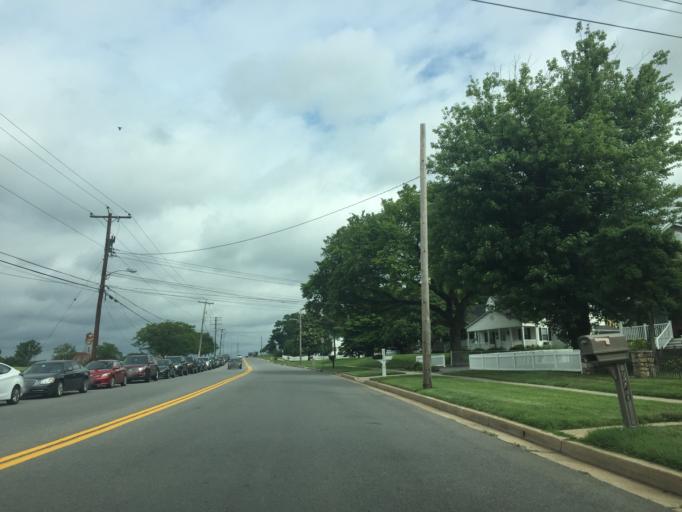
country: US
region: Maryland
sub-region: Baltimore County
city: Dundalk
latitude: 39.2617
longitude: -76.5131
